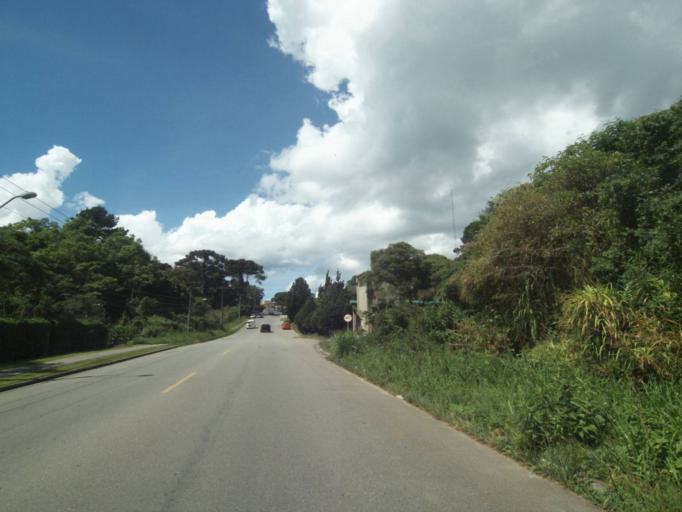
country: BR
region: Parana
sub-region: Curitiba
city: Curitiba
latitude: -25.4331
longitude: -49.3345
